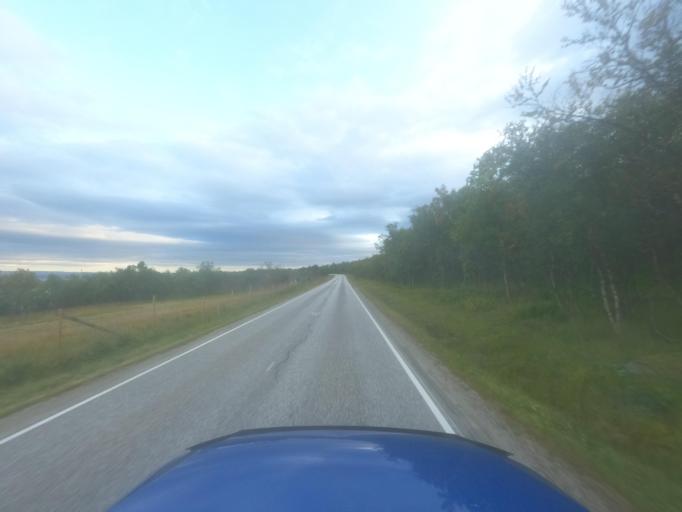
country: NO
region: Finnmark Fylke
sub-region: Porsanger
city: Lakselv
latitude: 70.4720
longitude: 25.2219
